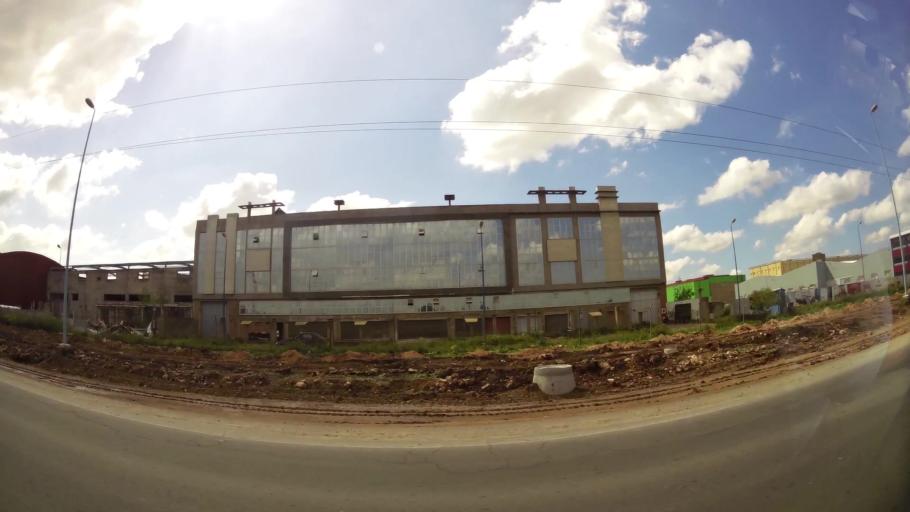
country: MA
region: Grand Casablanca
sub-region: Mediouna
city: Mediouna
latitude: 33.3927
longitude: -7.5354
